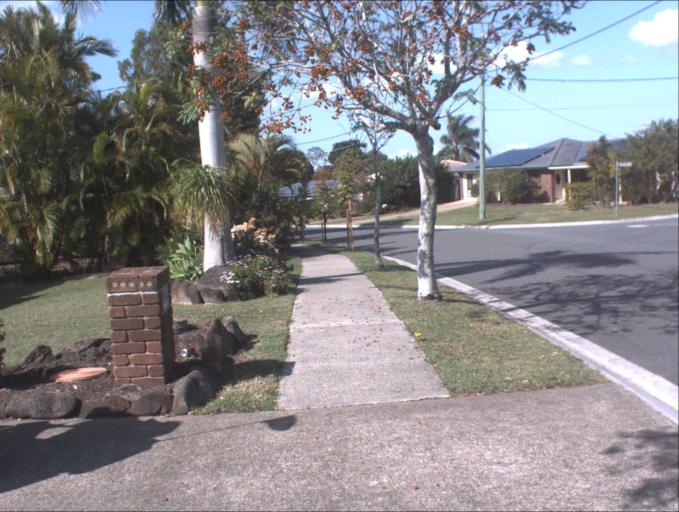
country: AU
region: Queensland
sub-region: Logan
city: Park Ridge South
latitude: -27.6943
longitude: 153.0151
